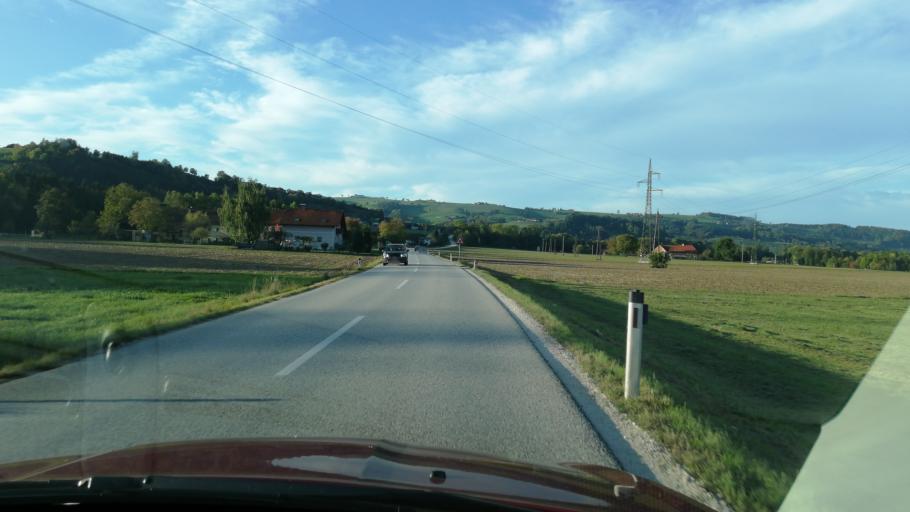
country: AT
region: Upper Austria
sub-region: Politischer Bezirk Steyr-Land
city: Ternberg
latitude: 47.9572
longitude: 14.3516
